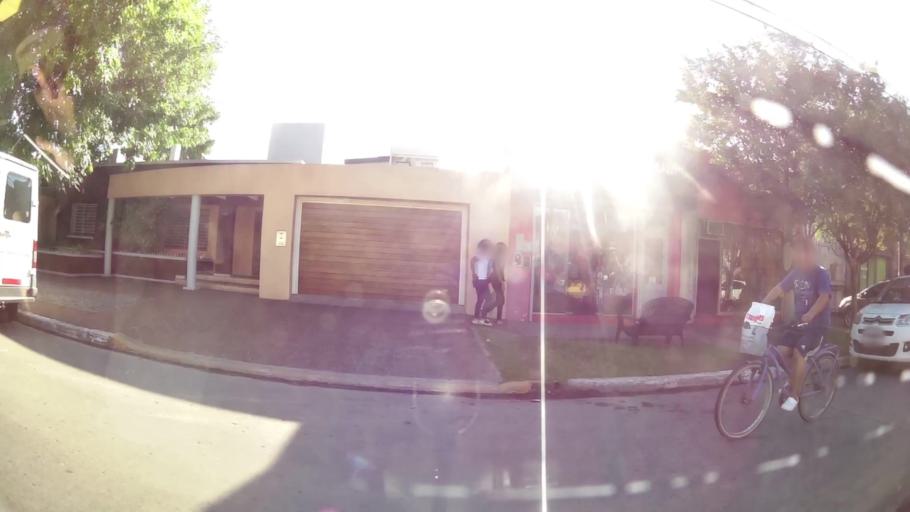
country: AR
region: Buenos Aires
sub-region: Partido de Merlo
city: Merlo
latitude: -34.6698
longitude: -58.7266
